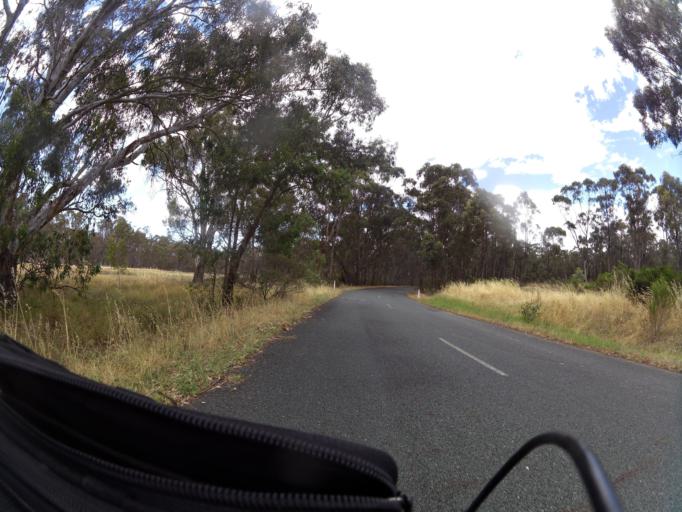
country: AU
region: Victoria
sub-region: Greater Shepparton
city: Shepparton
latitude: -36.6872
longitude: 145.1803
